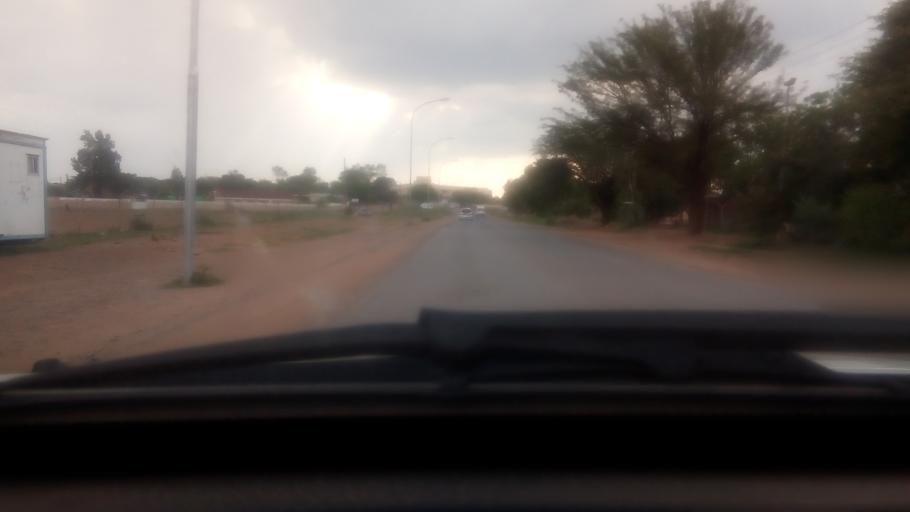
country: BW
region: Kweneng
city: Molepolole
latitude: -24.4107
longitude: 25.4923
